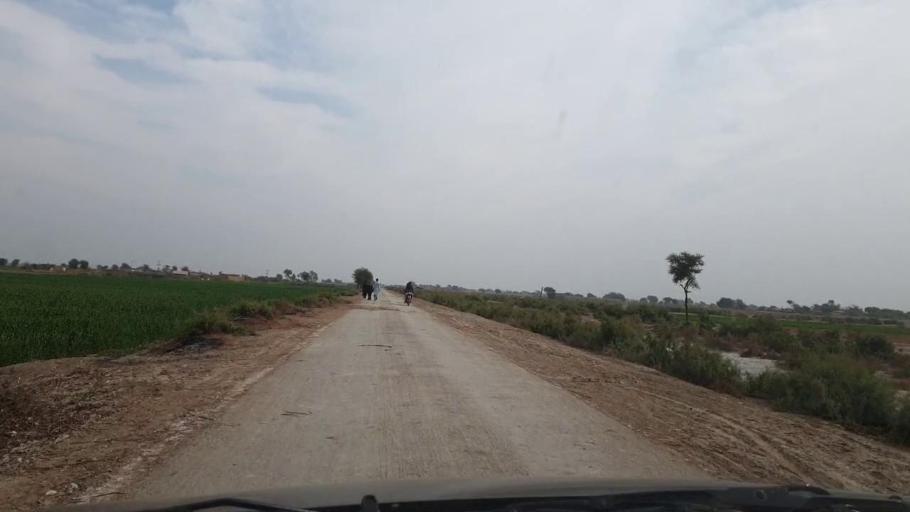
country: PK
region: Sindh
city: Sinjhoro
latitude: 26.0786
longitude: 68.8424
